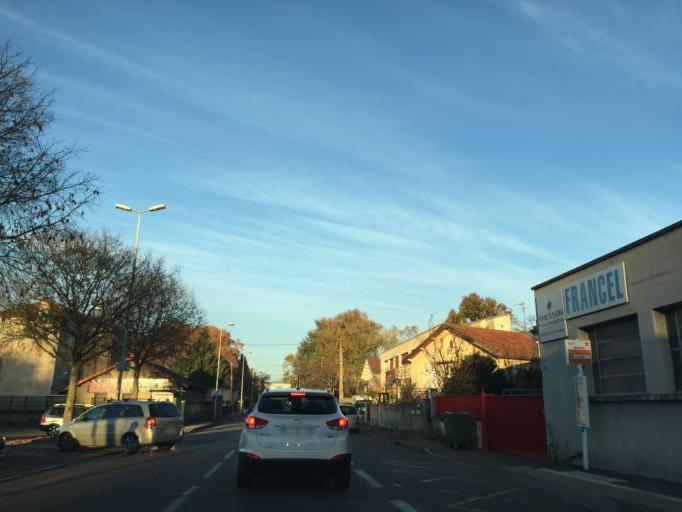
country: FR
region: Rhone-Alpes
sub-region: Departement de la Loire
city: Roanne
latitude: 46.0328
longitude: 4.0586
